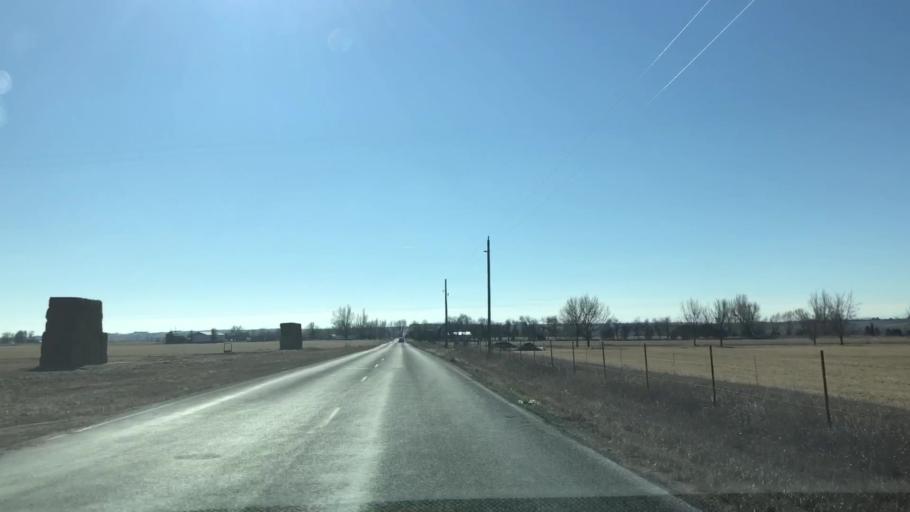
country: US
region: Colorado
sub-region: Weld County
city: Windsor
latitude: 40.4972
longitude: -104.9442
